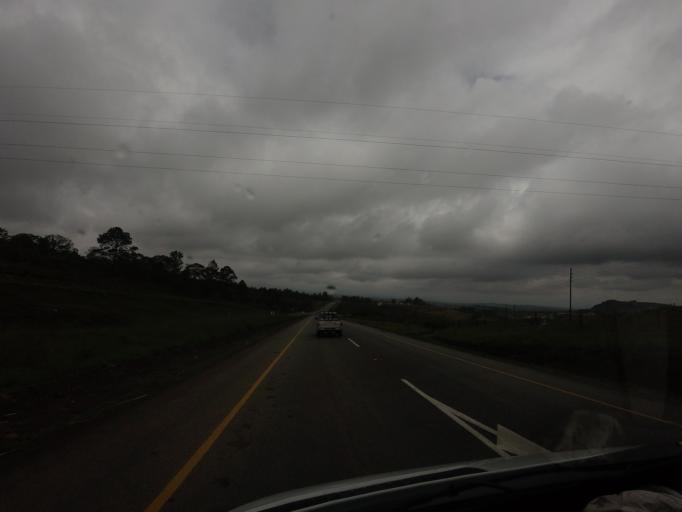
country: SZ
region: Hhohho
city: Lobamba
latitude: -26.5070
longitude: 31.2471
